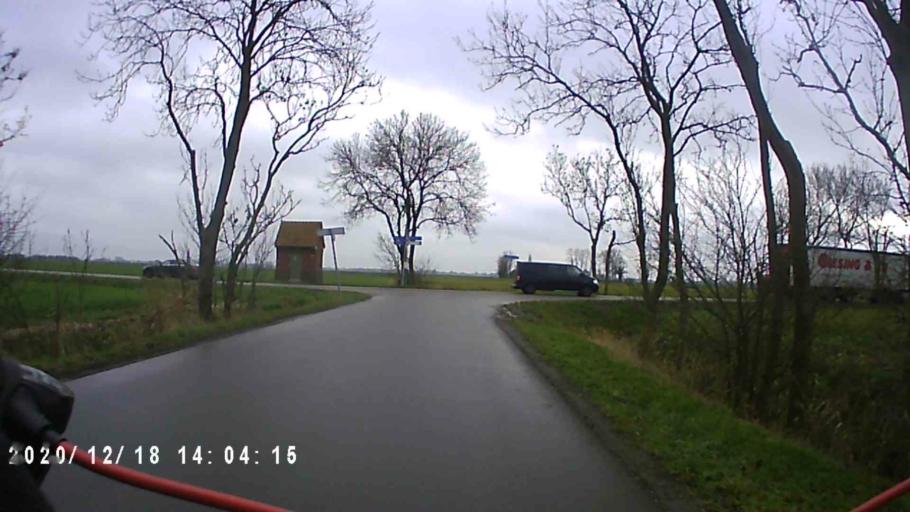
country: NL
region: Groningen
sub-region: Gemeente Bedum
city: Bedum
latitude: 53.2927
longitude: 6.6530
